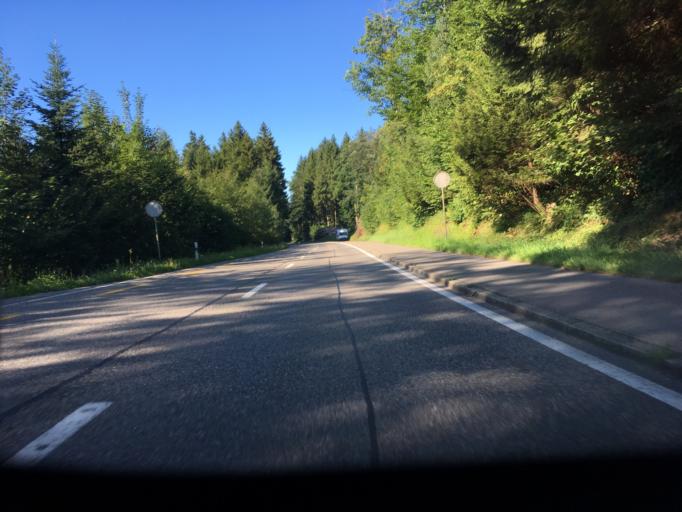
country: CH
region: Zug
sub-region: Zug
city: Baar
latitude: 47.2056
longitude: 8.5456
